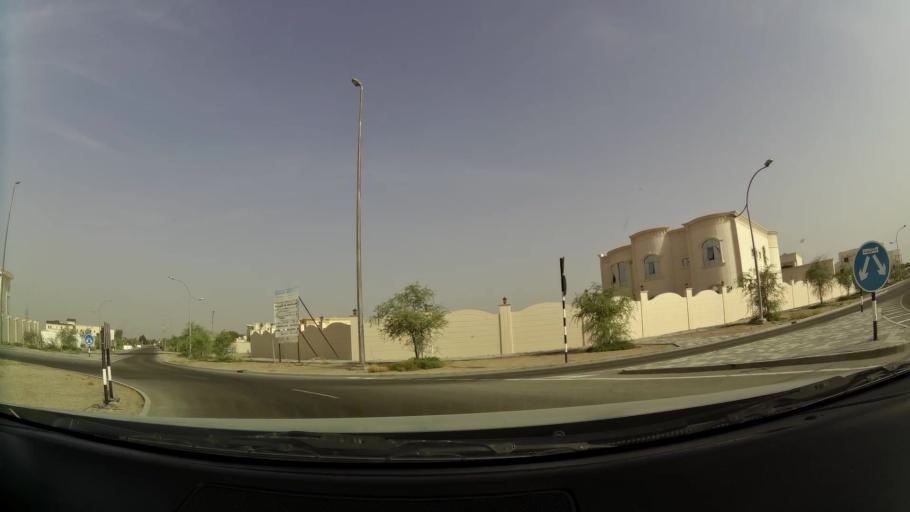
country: AE
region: Abu Dhabi
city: Al Ain
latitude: 24.1385
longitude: 55.7241
